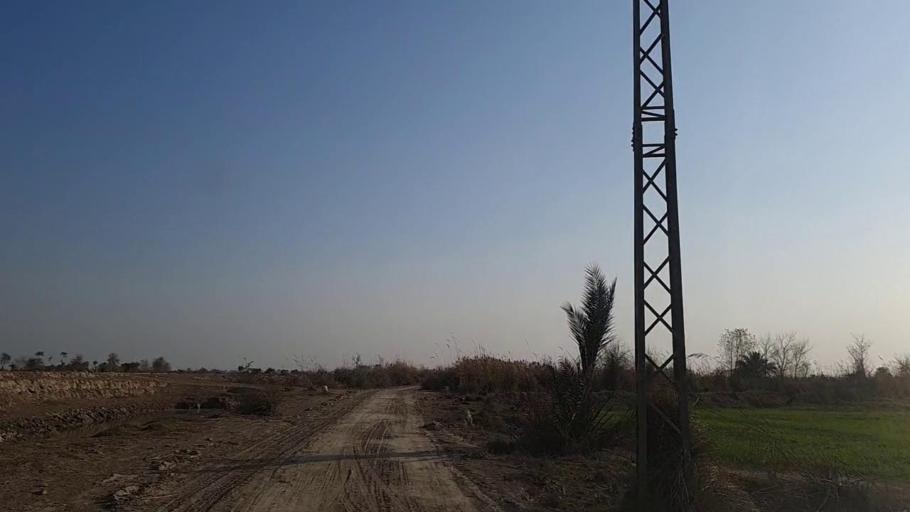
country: PK
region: Sindh
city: Daur
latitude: 26.4358
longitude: 68.3524
